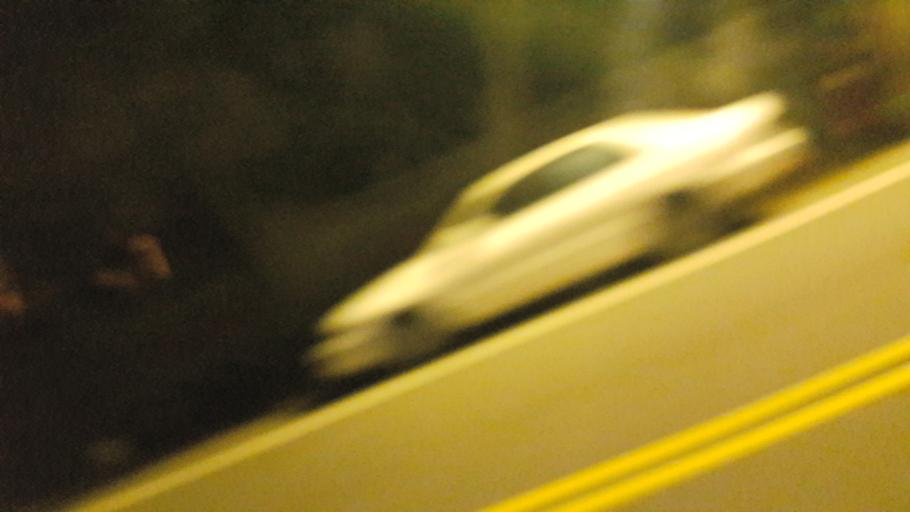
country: TW
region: Taiwan
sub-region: Hsinchu
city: Hsinchu
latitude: 24.7648
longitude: 120.9908
